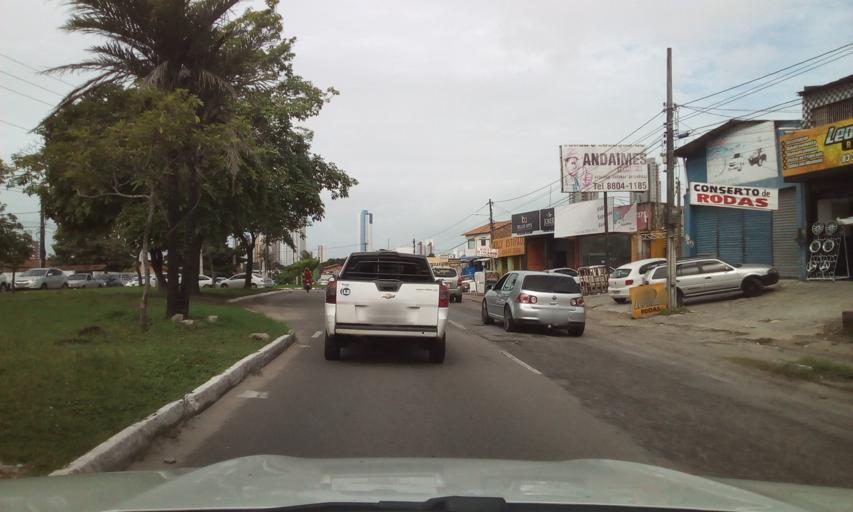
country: BR
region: Paraiba
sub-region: Joao Pessoa
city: Joao Pessoa
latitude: -7.0983
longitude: -34.8537
